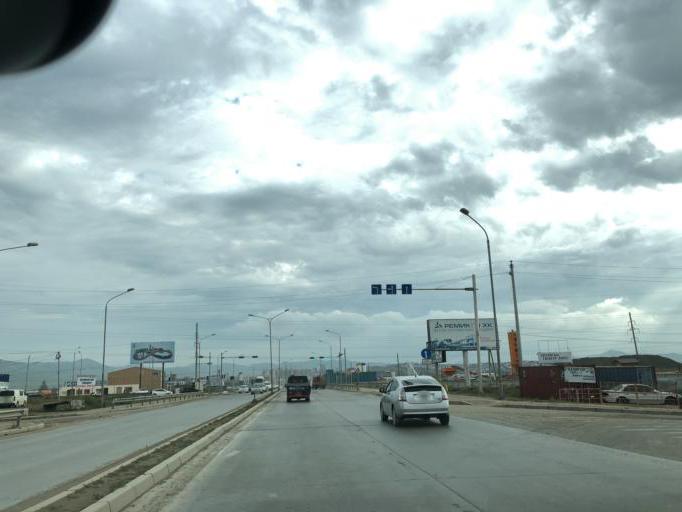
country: MN
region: Ulaanbaatar
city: Ulaanbaatar
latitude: 47.8917
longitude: 106.7853
